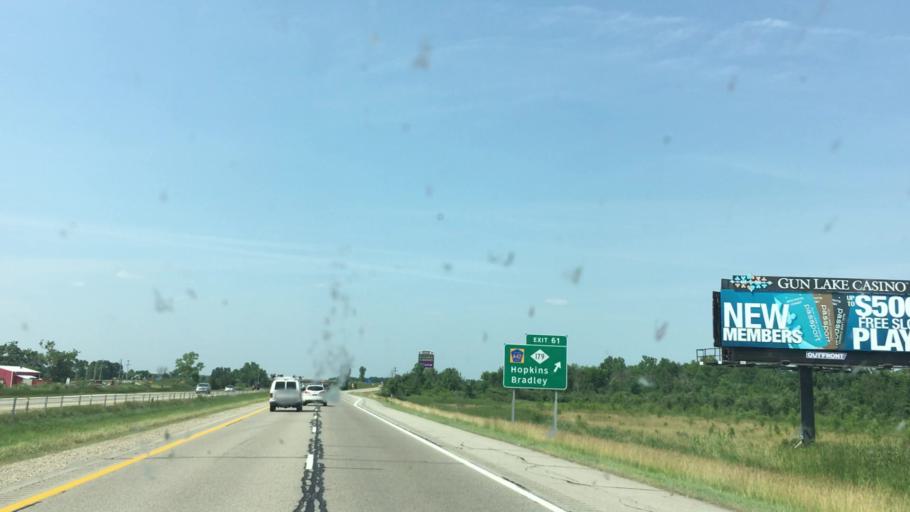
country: US
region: Michigan
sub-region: Allegan County
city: Wayland
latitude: 42.6245
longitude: -85.6622
